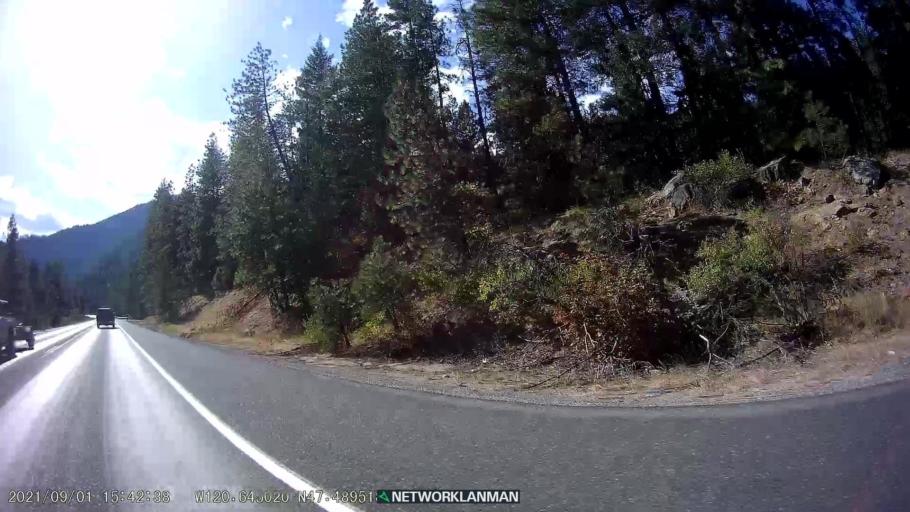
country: US
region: Washington
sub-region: Chelan County
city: Leavenworth
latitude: 47.4894
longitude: -120.6456
